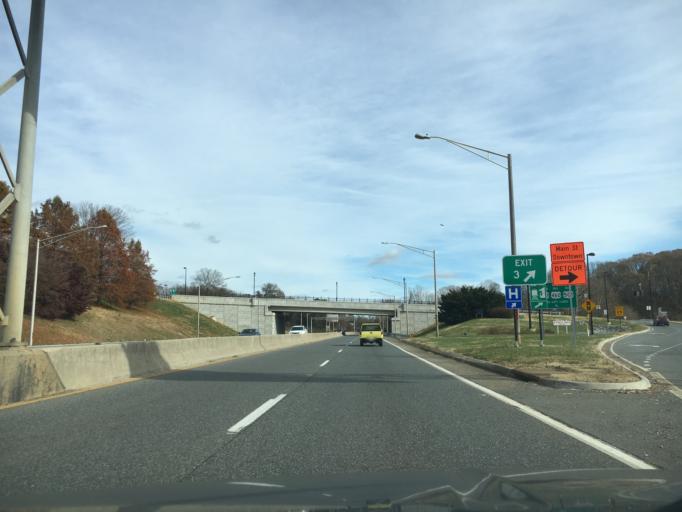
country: US
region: Virginia
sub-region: City of Lynchburg
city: Lynchburg
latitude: 37.3989
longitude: -79.1523
